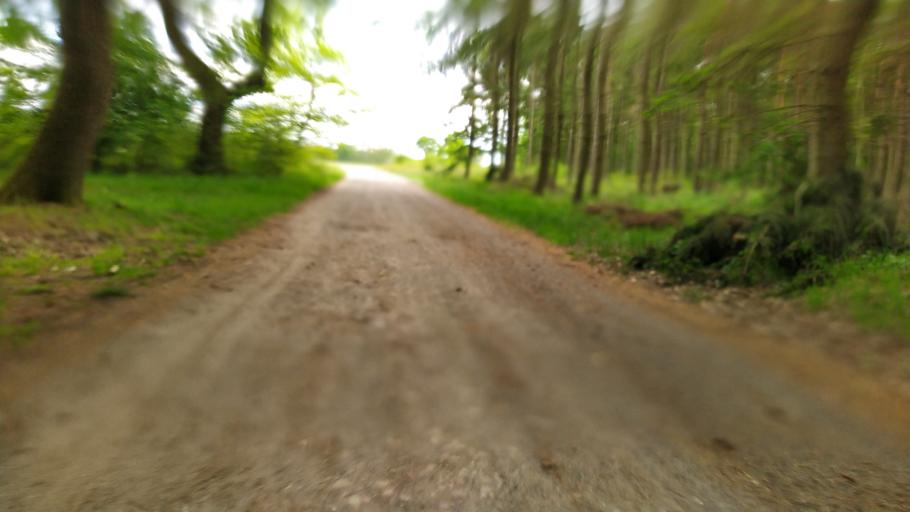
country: DE
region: Lower Saxony
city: Ahlerstedt
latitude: 53.3688
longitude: 9.3941
